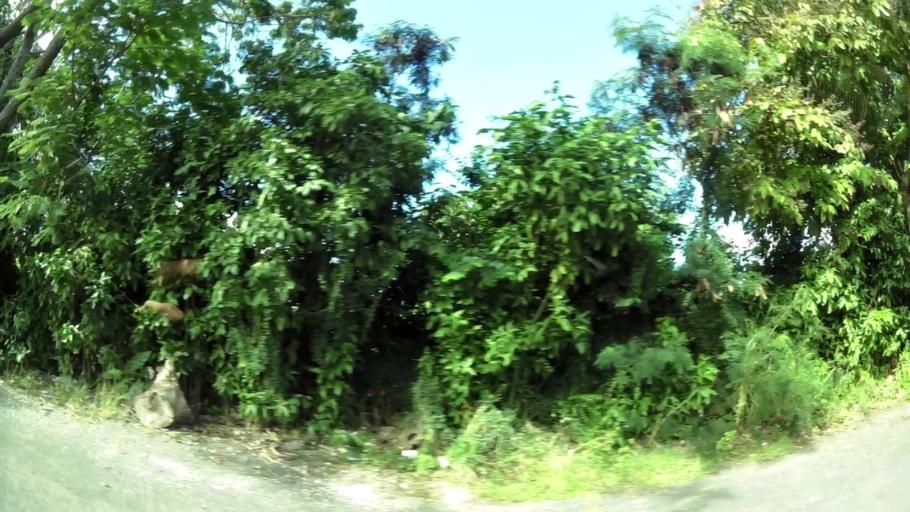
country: GP
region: Guadeloupe
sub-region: Guadeloupe
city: Port-Louis
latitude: 16.4169
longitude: -61.5268
